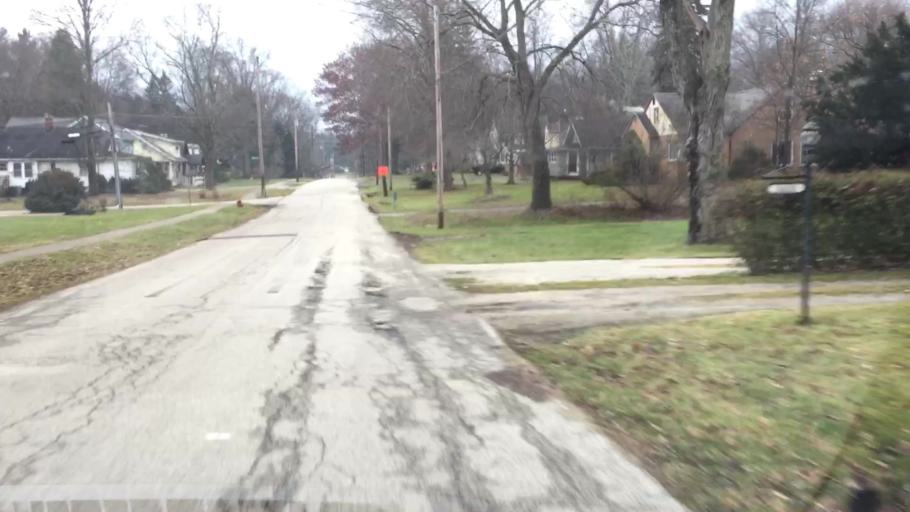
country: US
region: Ohio
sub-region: Summit County
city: Stow
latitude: 41.1638
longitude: -81.4382
